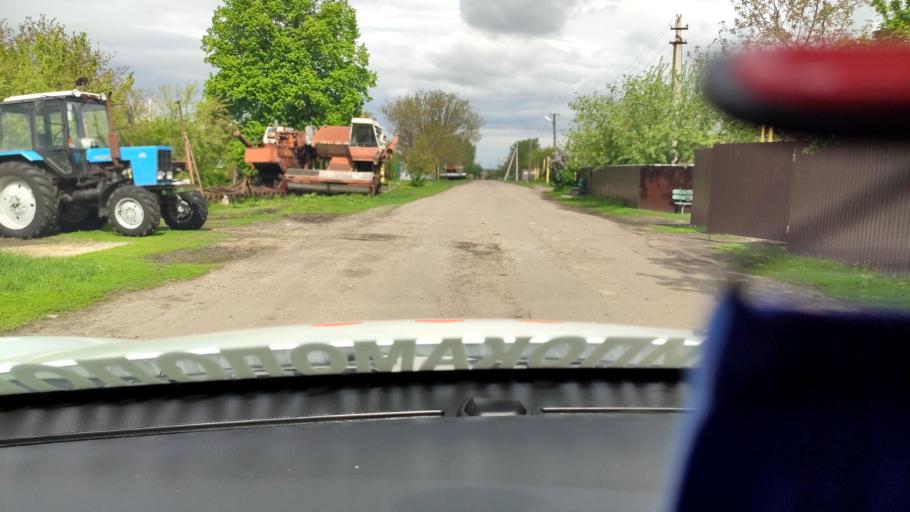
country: RU
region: Voronezj
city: Imeni Pervogo Maya
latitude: 50.6913
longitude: 39.5157
